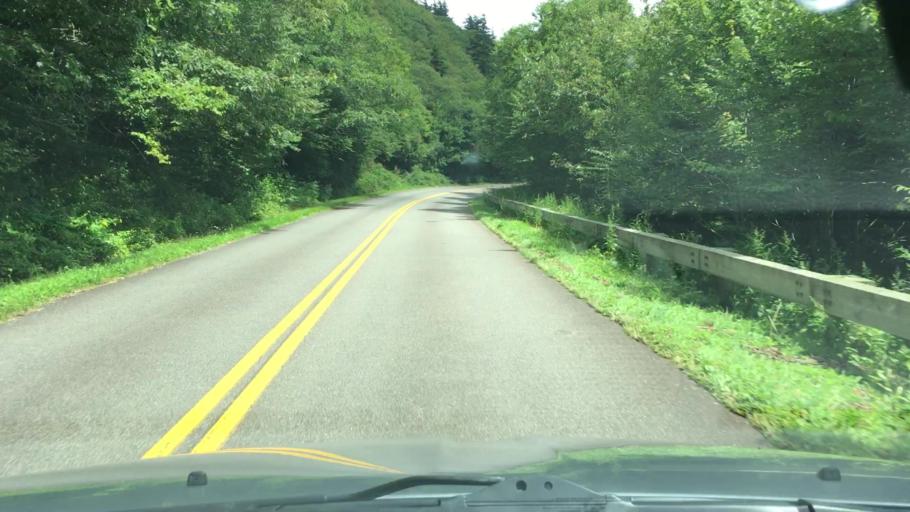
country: US
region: North Carolina
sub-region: Buncombe County
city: Black Mountain
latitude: 35.7213
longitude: -82.2828
